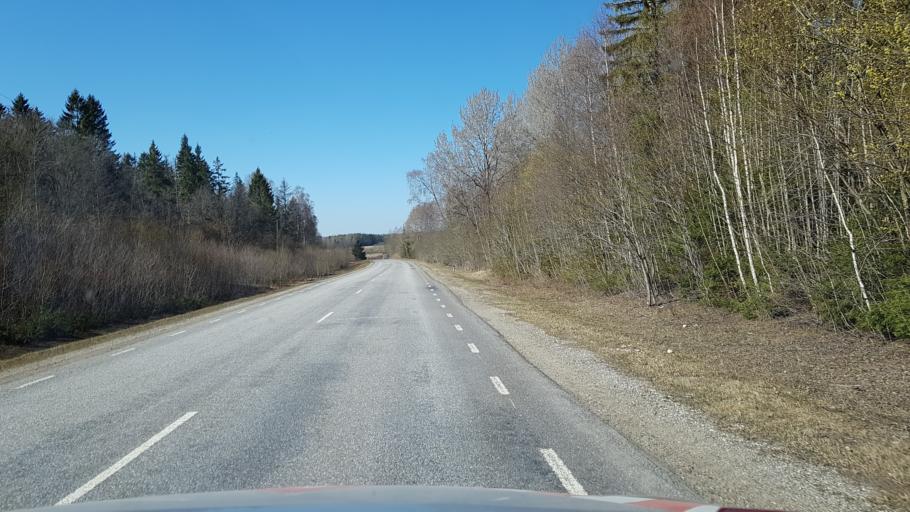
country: EE
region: Laeaene-Virumaa
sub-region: Vaeike-Maarja vald
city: Vaike-Maarja
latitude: 59.1537
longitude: 26.2180
